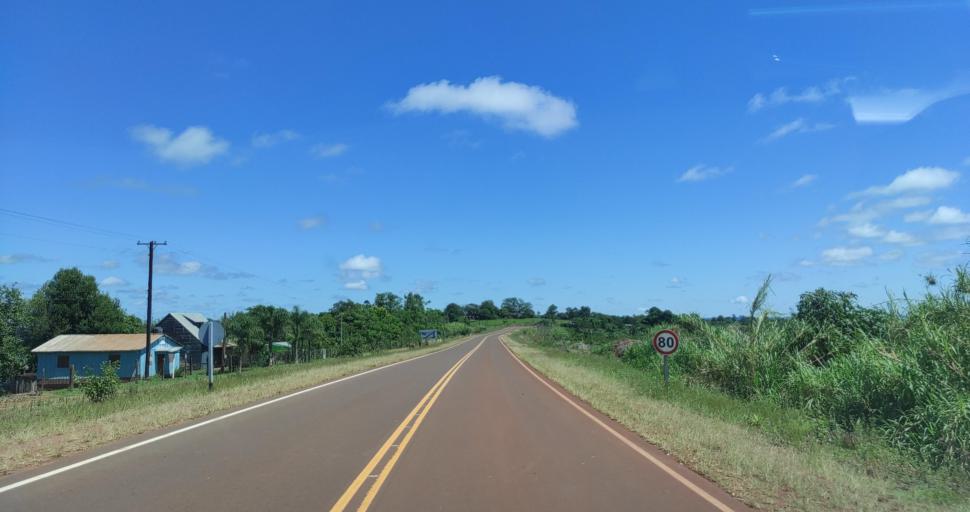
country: AR
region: Misiones
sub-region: Departamento de Veinticinco de Mayo
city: Veinticinco de Mayo
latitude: -27.3405
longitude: -54.8849
